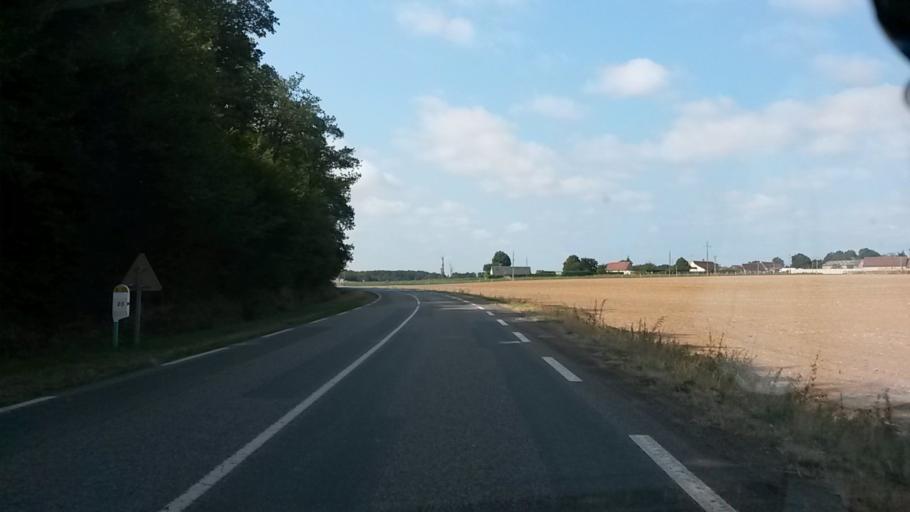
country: FR
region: Haute-Normandie
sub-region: Departement de l'Eure
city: Damville
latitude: 48.8337
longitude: 1.0226
